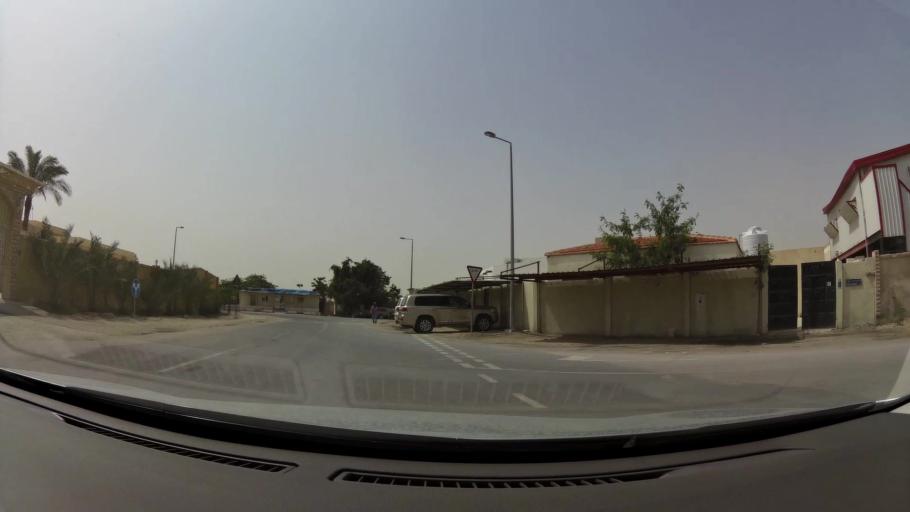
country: QA
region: Baladiyat ar Rayyan
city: Ar Rayyan
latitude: 25.2356
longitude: 51.4274
